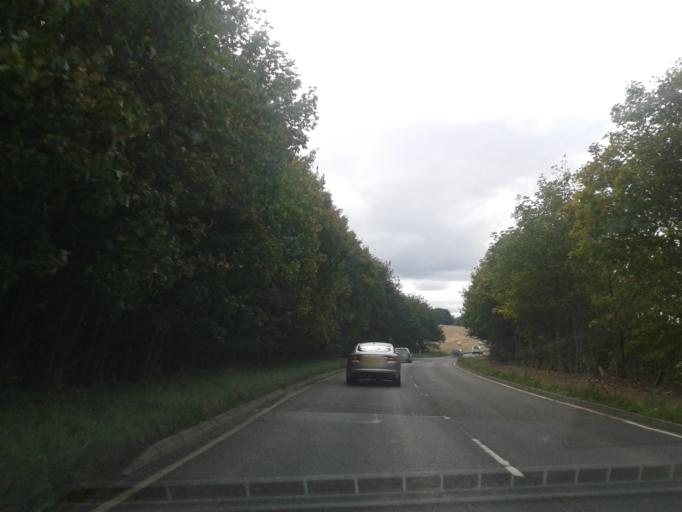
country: GB
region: Scotland
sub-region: Fife
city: Balmullo
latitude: 56.3510
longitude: -2.9301
